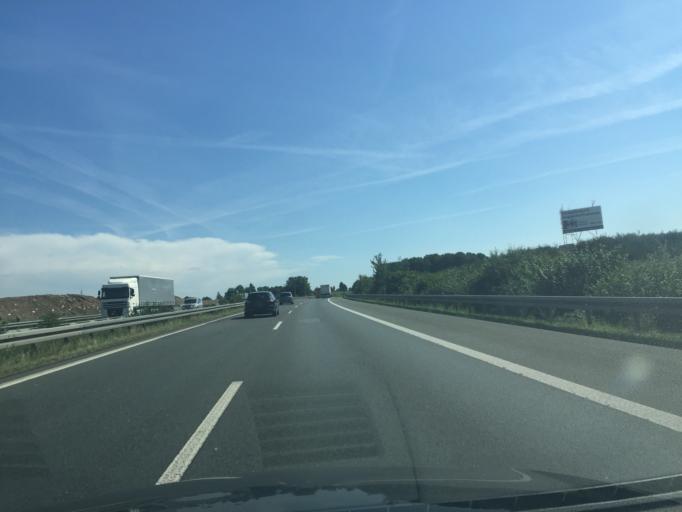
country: DE
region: North Rhine-Westphalia
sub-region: Regierungsbezirk Arnsberg
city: Olpe
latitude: 51.0259
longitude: 7.8276
